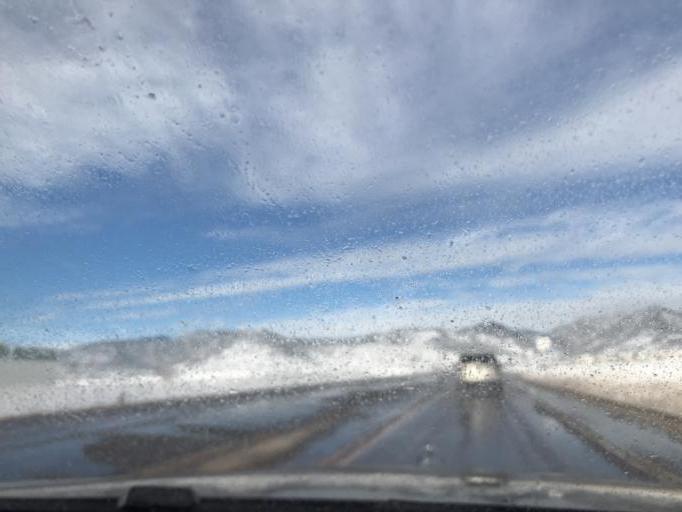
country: US
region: Colorado
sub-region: Boulder County
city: Superior
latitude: 39.8636
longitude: -105.2118
